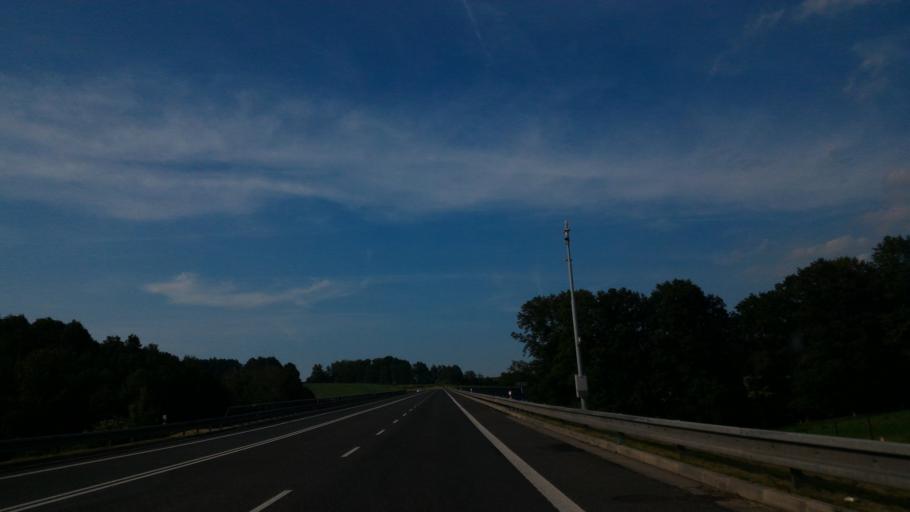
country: CZ
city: Chrastava
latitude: 50.8276
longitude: 14.9380
